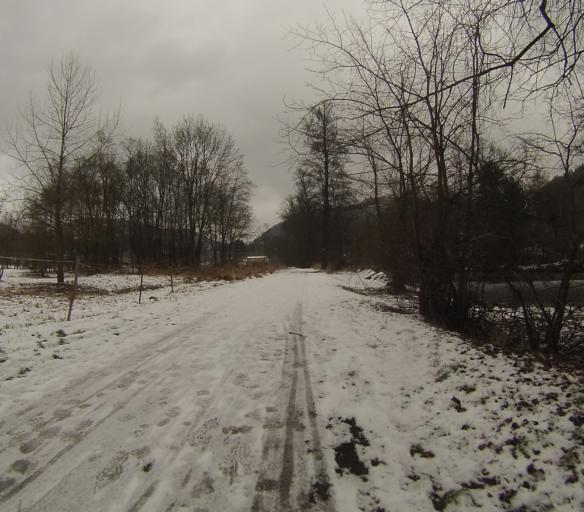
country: CZ
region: Ustecky
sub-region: Okres Decin
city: Decin
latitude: 50.7648
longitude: 14.2377
